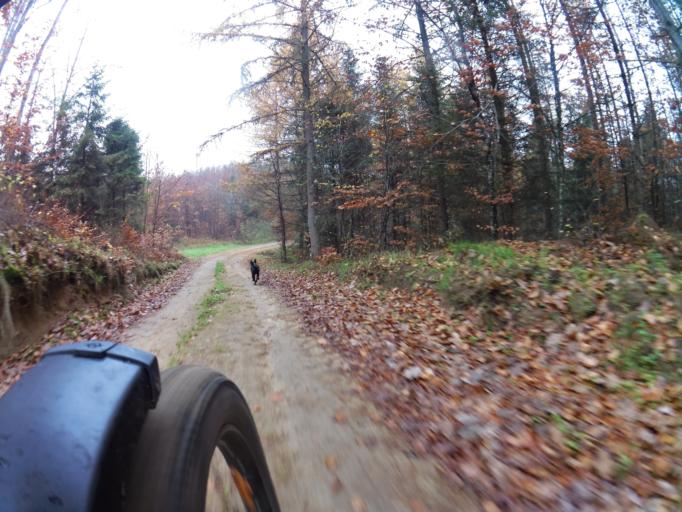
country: PL
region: Pomeranian Voivodeship
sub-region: Powiat wejherowski
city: Orle
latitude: 54.6986
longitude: 18.1556
